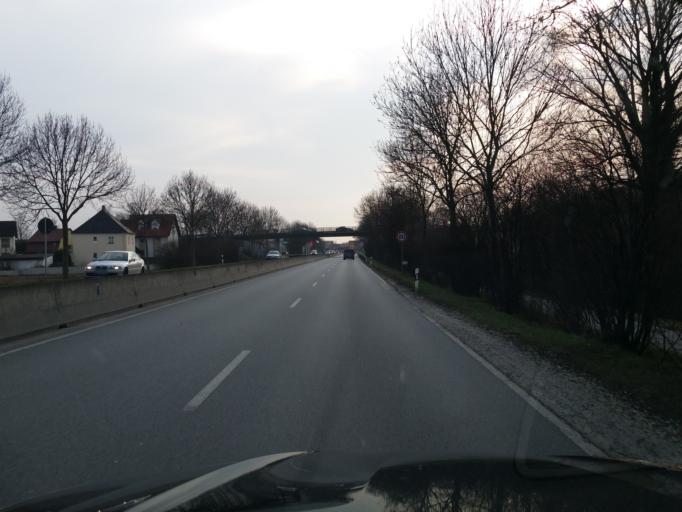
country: DE
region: Bavaria
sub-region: Lower Bavaria
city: Ergolding
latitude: 48.5609
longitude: 12.1702
